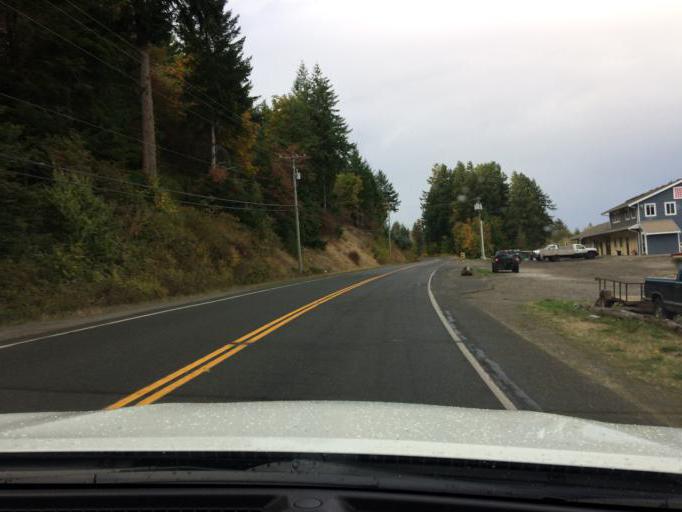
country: CA
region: British Columbia
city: Cumberland
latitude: 49.5133
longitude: -124.8352
